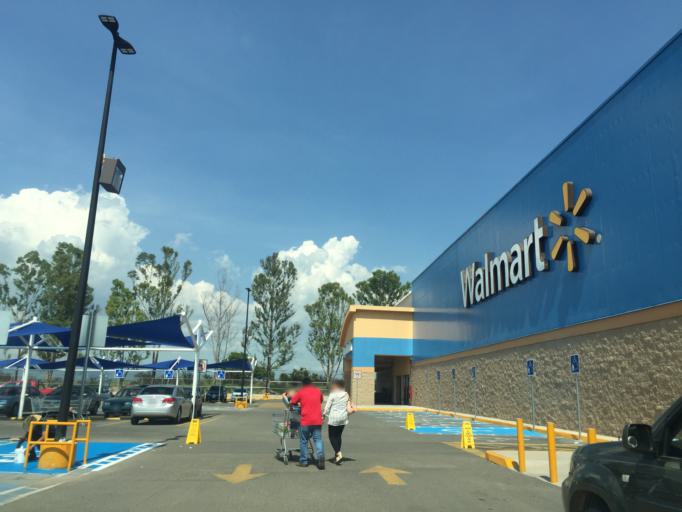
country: MX
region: Guanajuato
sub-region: Leon
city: La Ermita
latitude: 21.1728
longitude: -101.7329
